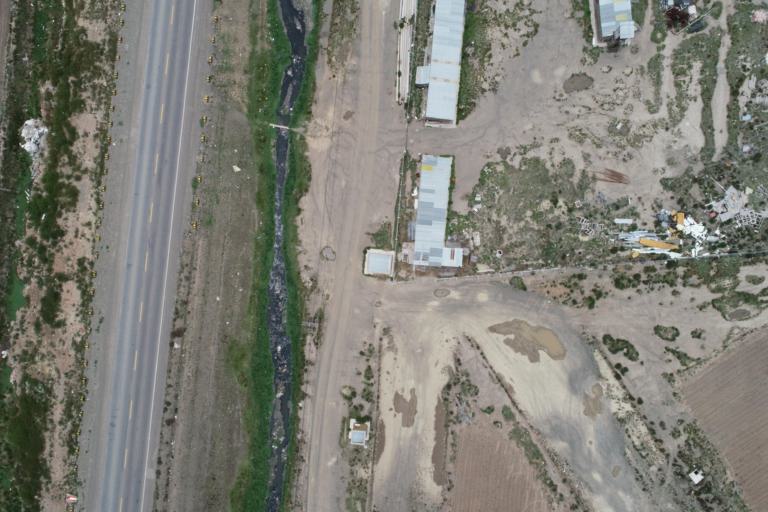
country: BO
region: La Paz
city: La Paz
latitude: -16.5217
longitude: -68.2979
